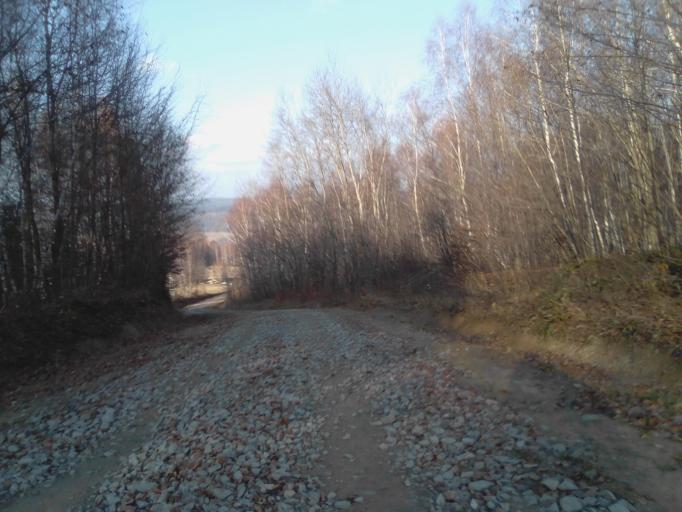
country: PL
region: Subcarpathian Voivodeship
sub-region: Powiat strzyzowski
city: Gwoznica Gorna
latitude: 49.8267
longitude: 21.9820
